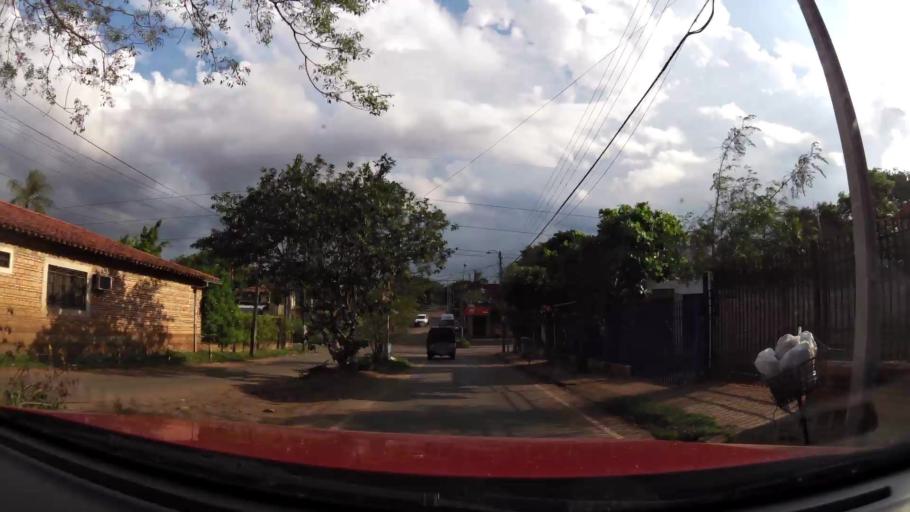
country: PY
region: Central
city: Fernando de la Mora
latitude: -25.3564
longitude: -57.5547
